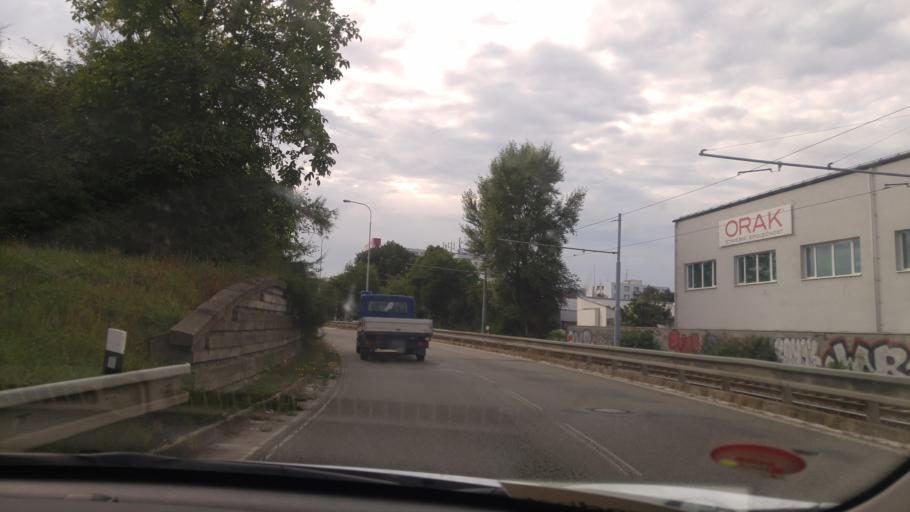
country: CZ
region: South Moravian
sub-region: Mesto Brno
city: Brno
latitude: 49.2116
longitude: 16.5702
